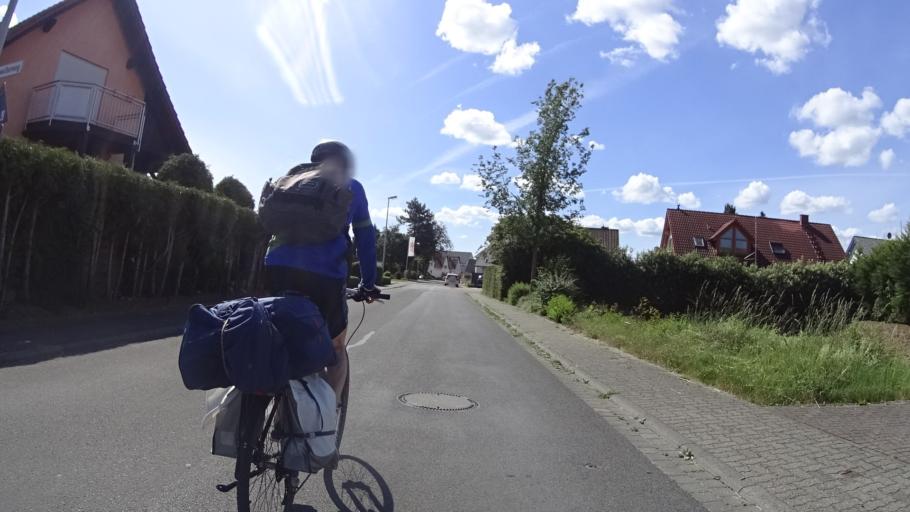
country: DE
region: Bavaria
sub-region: Regierungsbezirk Unterfranken
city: Niedernberg
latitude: 49.9198
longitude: 9.1395
